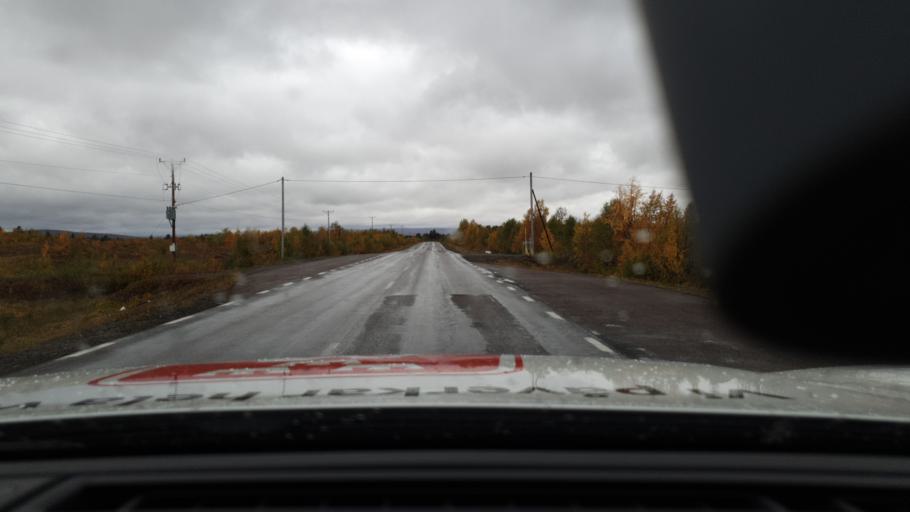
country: SE
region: Norrbotten
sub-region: Kiruna Kommun
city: Kiruna
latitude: 67.7665
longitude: 20.1501
